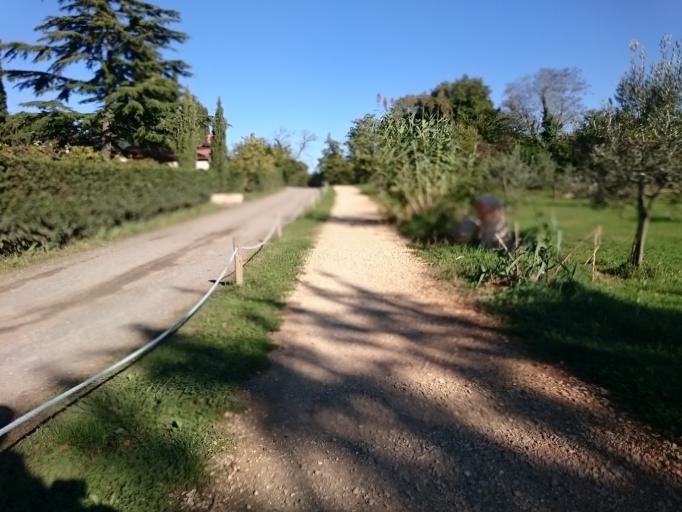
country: HR
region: Istarska
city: Novigrad
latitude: 45.3374
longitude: 13.5416
